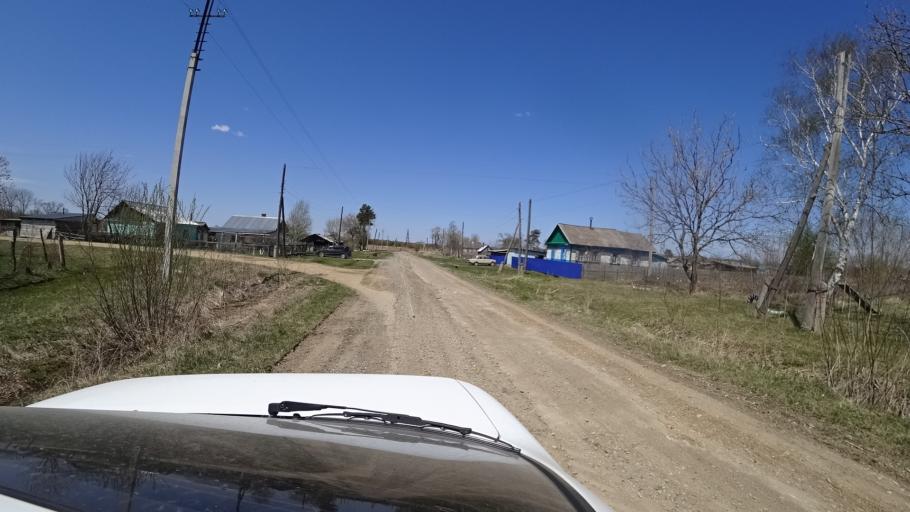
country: RU
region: Primorskiy
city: Lazo
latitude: 45.8008
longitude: 133.7629
